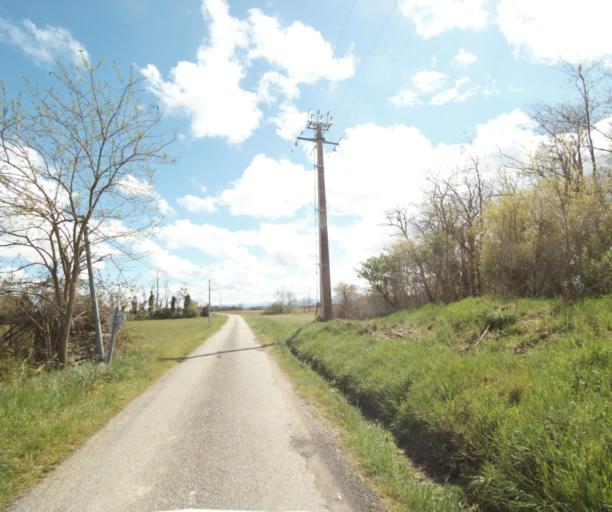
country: FR
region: Midi-Pyrenees
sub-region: Departement de l'Ariege
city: Saverdun
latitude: 43.2587
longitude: 1.5961
